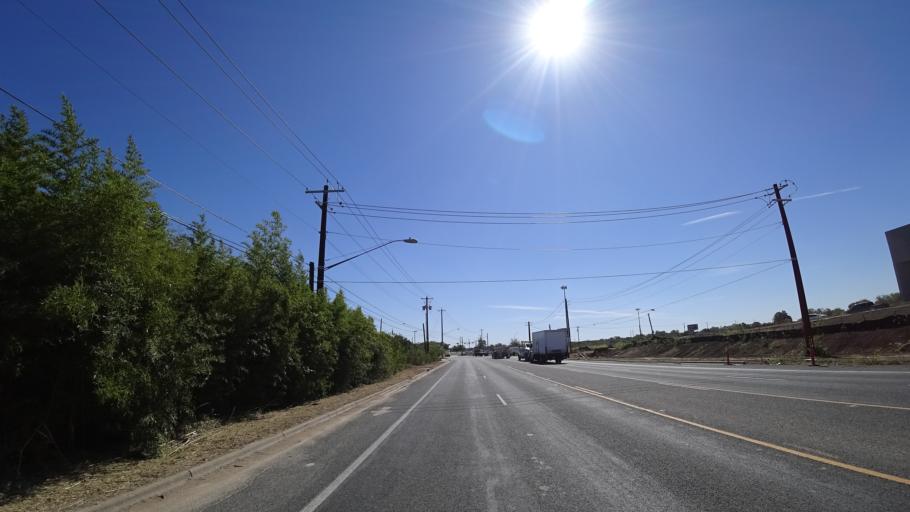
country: US
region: Texas
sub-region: Travis County
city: Austin
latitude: 30.1838
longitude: -97.6889
